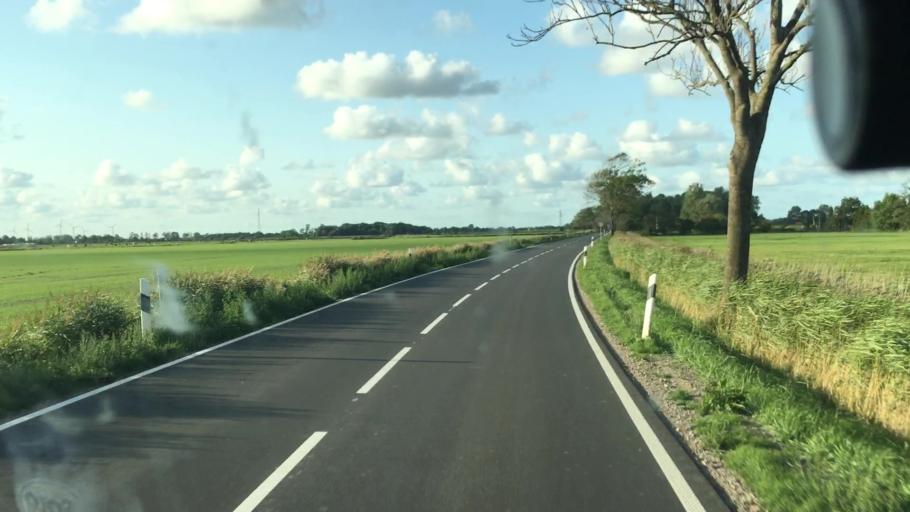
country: DE
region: Lower Saxony
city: Jever
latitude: 53.6270
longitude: 7.8618
